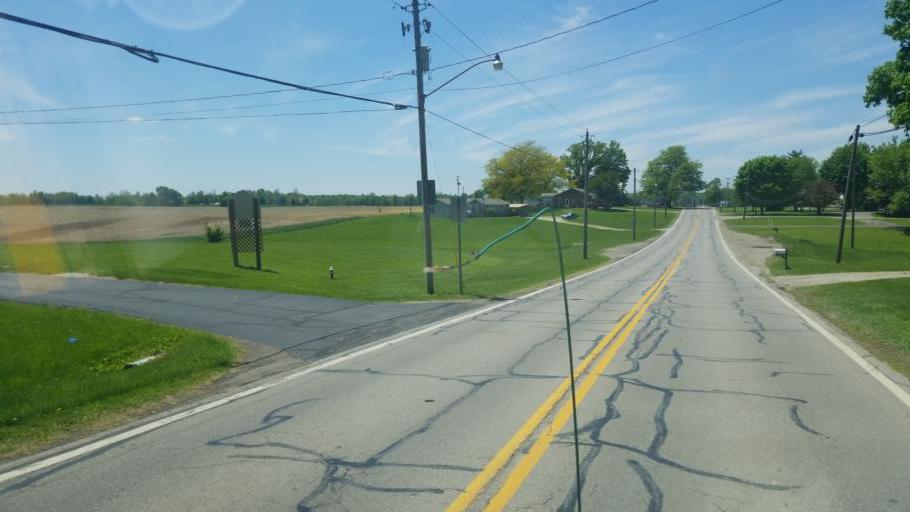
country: US
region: Ohio
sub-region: Huron County
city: Greenwich
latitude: 41.0300
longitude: -82.5264
